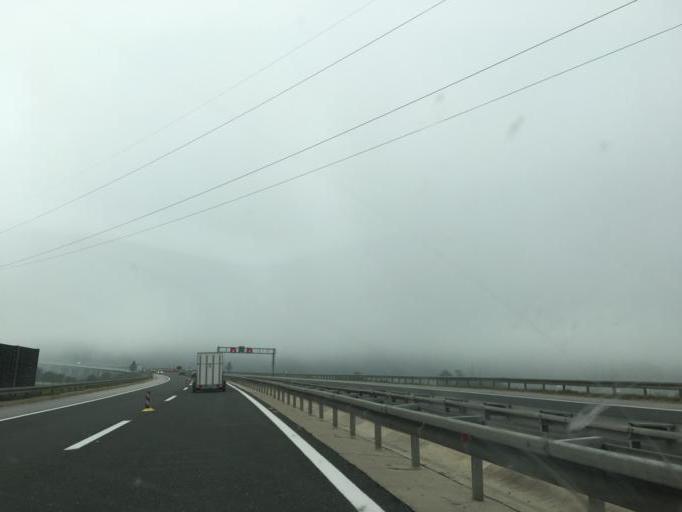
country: HR
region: Licko-Senjska
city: Otocac
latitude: 44.8669
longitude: 15.2079
